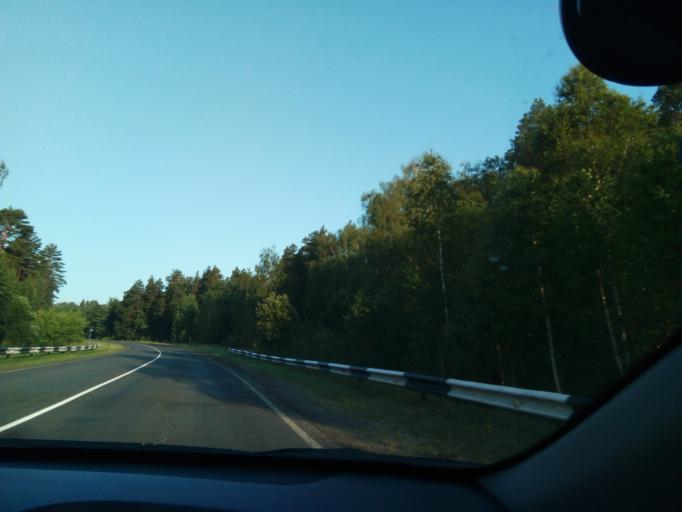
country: RU
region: Nizjnij Novgorod
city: Satis
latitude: 54.9351
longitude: 43.2231
